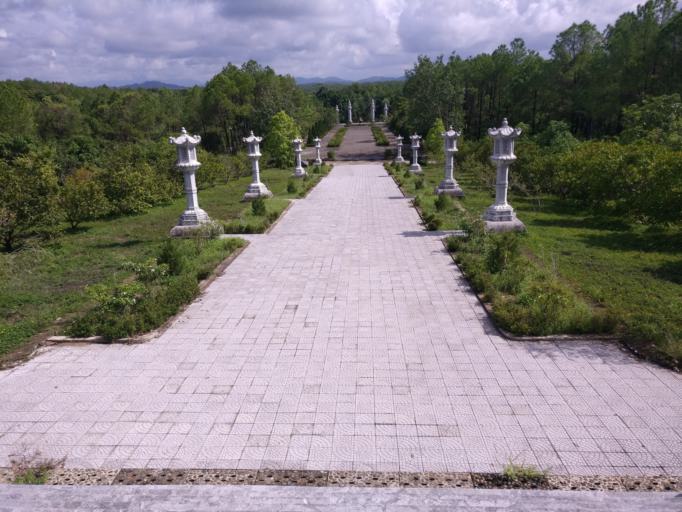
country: VN
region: Thua Thien-Hue
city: Hue
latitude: 16.4205
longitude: 107.6089
